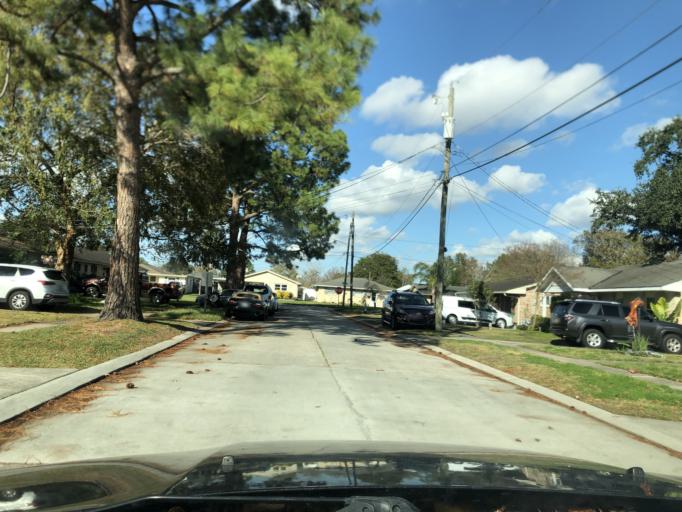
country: US
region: Louisiana
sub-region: Jefferson Parish
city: Metairie Terrace
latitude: 29.9849
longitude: -90.1653
